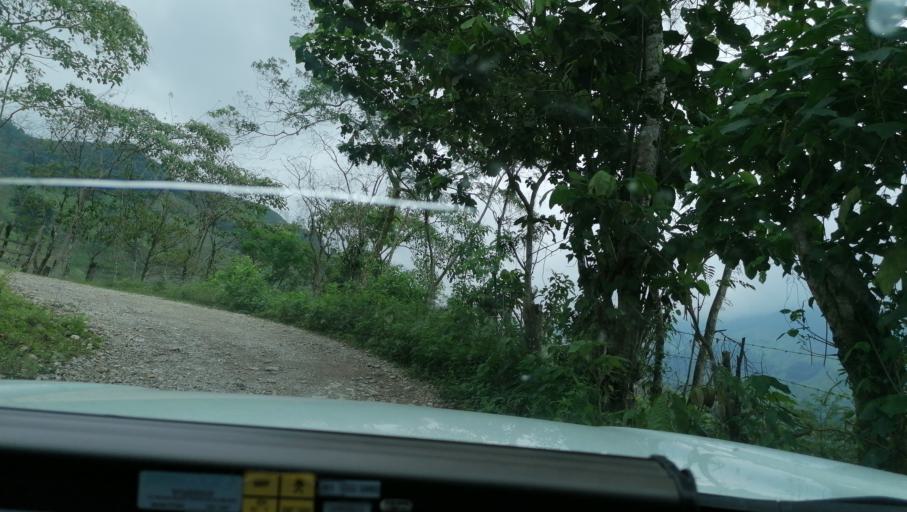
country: MX
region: Chiapas
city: Ocotepec
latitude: 17.3209
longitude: -93.1356
